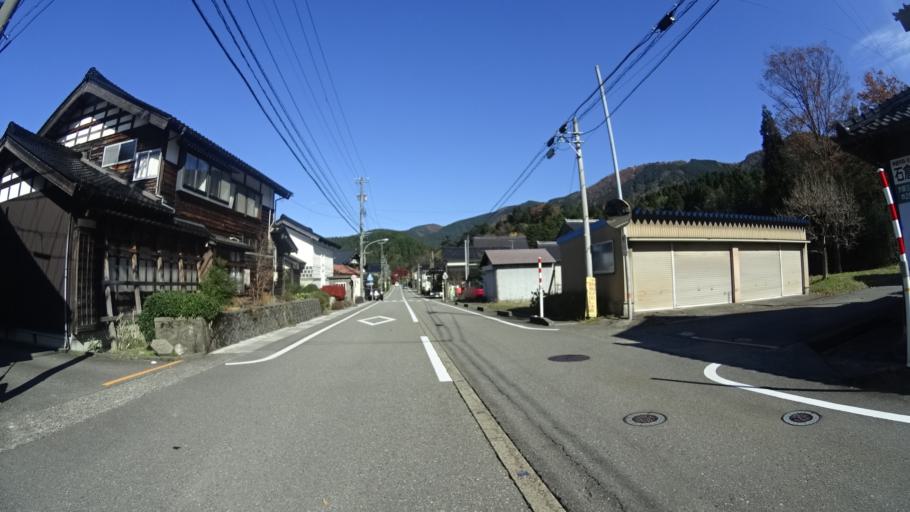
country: JP
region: Ishikawa
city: Tsurugi-asahimachi
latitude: 36.4316
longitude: 136.6339
